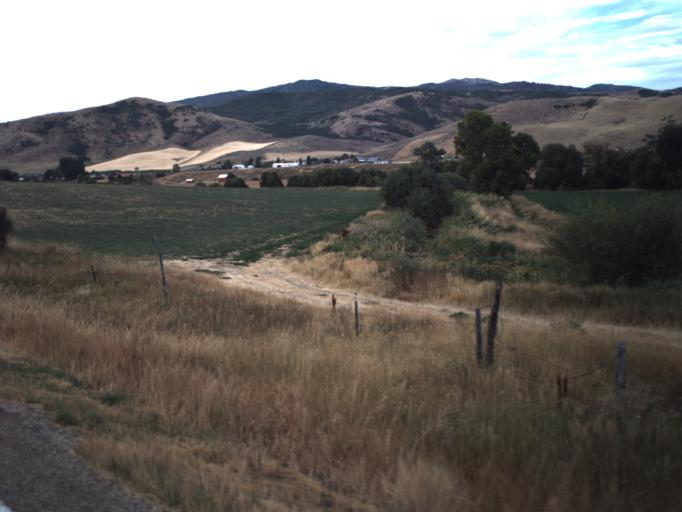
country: US
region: Utah
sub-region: Morgan County
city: Morgan
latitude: 41.0016
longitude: -111.6773
